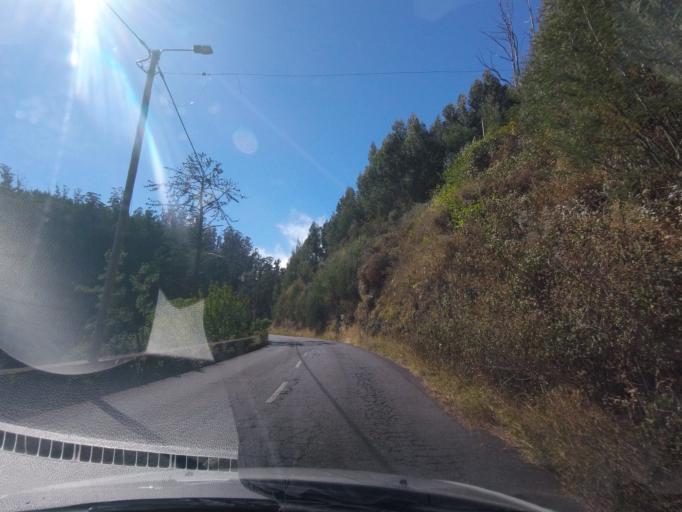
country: PT
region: Madeira
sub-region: Santa Cruz
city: Camacha
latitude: 32.6906
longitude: -16.8502
